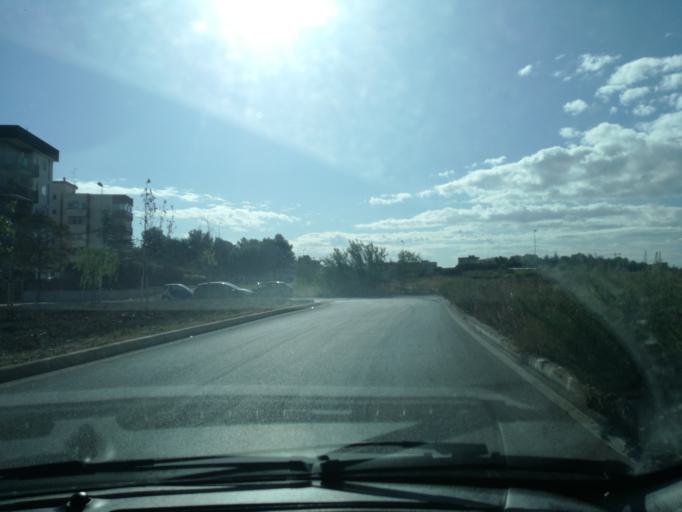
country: IT
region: Apulia
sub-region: Provincia di Bari
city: Triggiano
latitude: 41.0709
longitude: 16.9269
